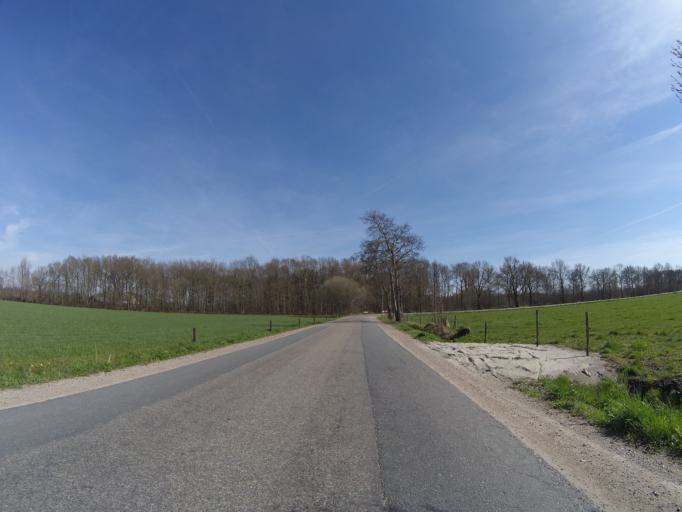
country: NL
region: Gelderland
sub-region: Gemeente Barneveld
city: Zwartebroek
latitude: 52.1953
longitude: 5.4980
